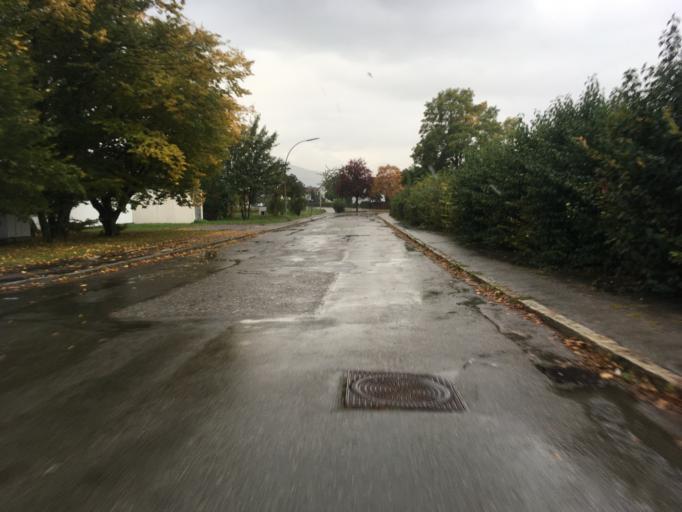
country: DE
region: Baden-Wuerttemberg
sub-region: Tuebingen Region
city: Nehren
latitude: 48.4139
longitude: 9.0697
